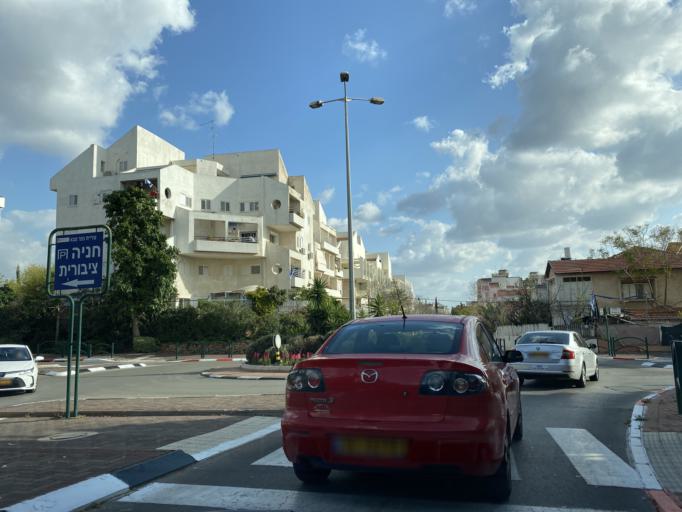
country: IL
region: Central District
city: Kfar Saba
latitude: 32.1819
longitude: 34.9195
